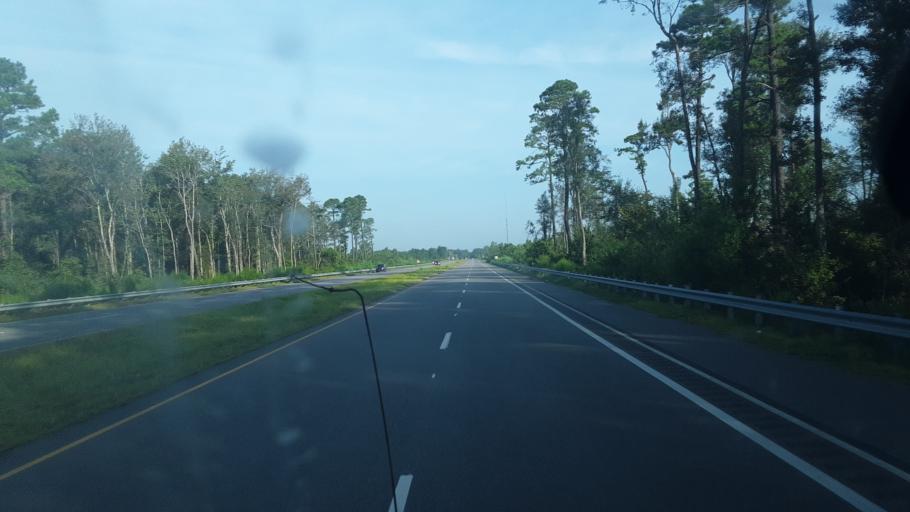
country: US
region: South Carolina
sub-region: Horry County
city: Forestbrook
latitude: 33.8080
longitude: -78.8949
